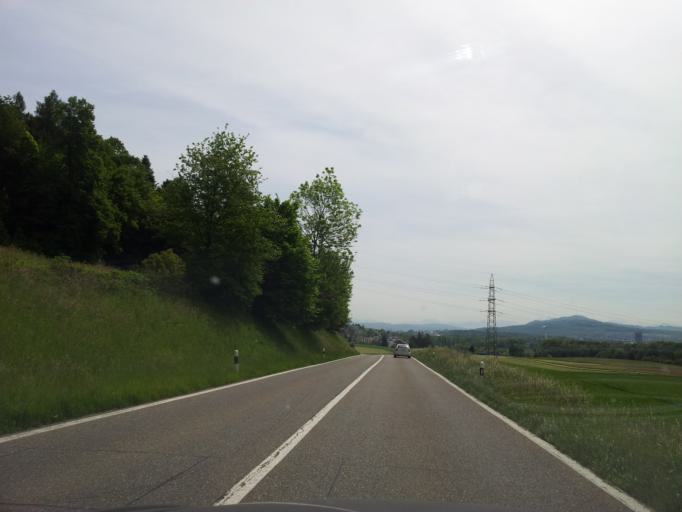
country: CH
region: Aargau
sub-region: Bezirk Baden
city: Wurenlos
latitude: 47.4339
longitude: 8.3771
